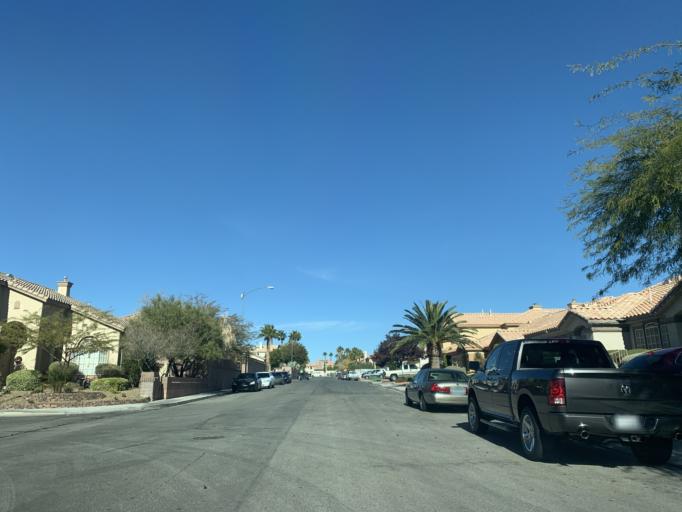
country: US
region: Nevada
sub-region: Clark County
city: Summerlin South
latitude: 36.1192
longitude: -115.2902
